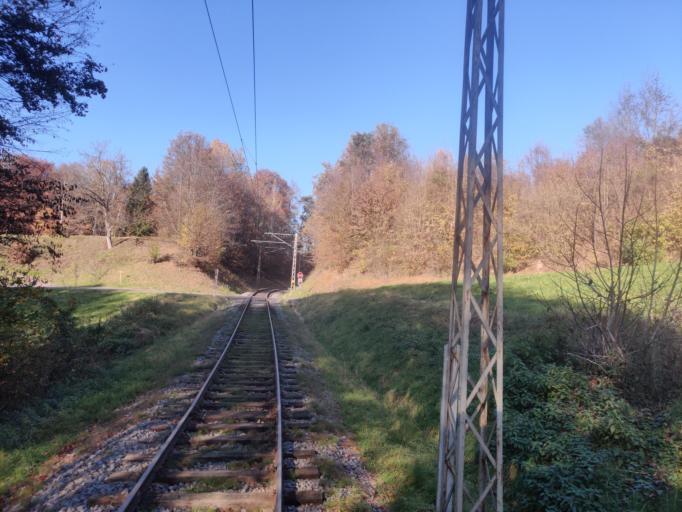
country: AT
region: Styria
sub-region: Politischer Bezirk Suedoststeiermark
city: Maierdorf
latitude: 46.8918
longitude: 15.8644
